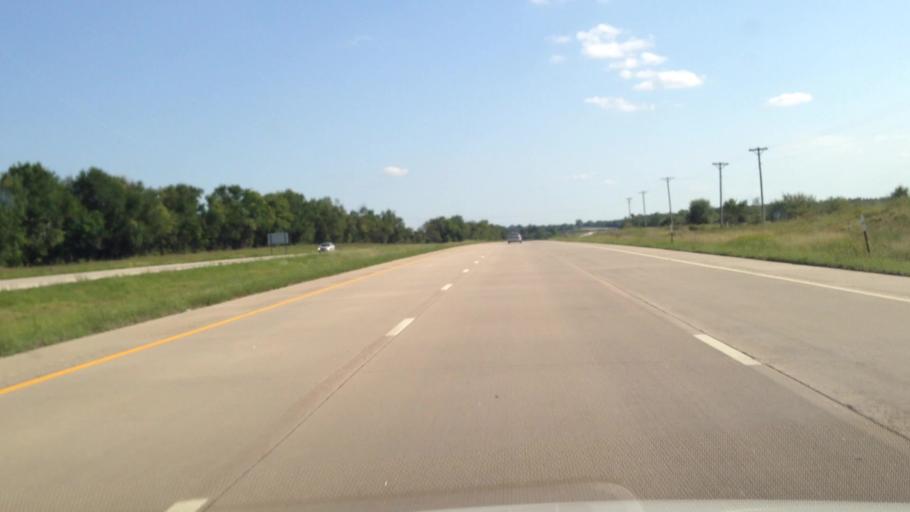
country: US
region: Kansas
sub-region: Bourbon County
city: Fort Scott
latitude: 37.8891
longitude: -94.7052
